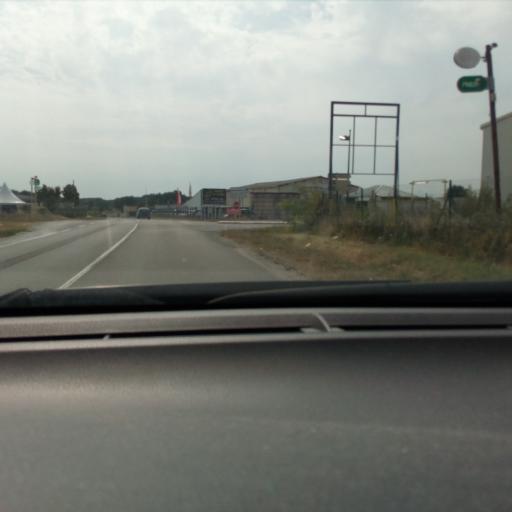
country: FR
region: Poitou-Charentes
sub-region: Departement de la Charente
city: Saint-Yrieix-sur-Charente
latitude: 45.6830
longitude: 0.1030
